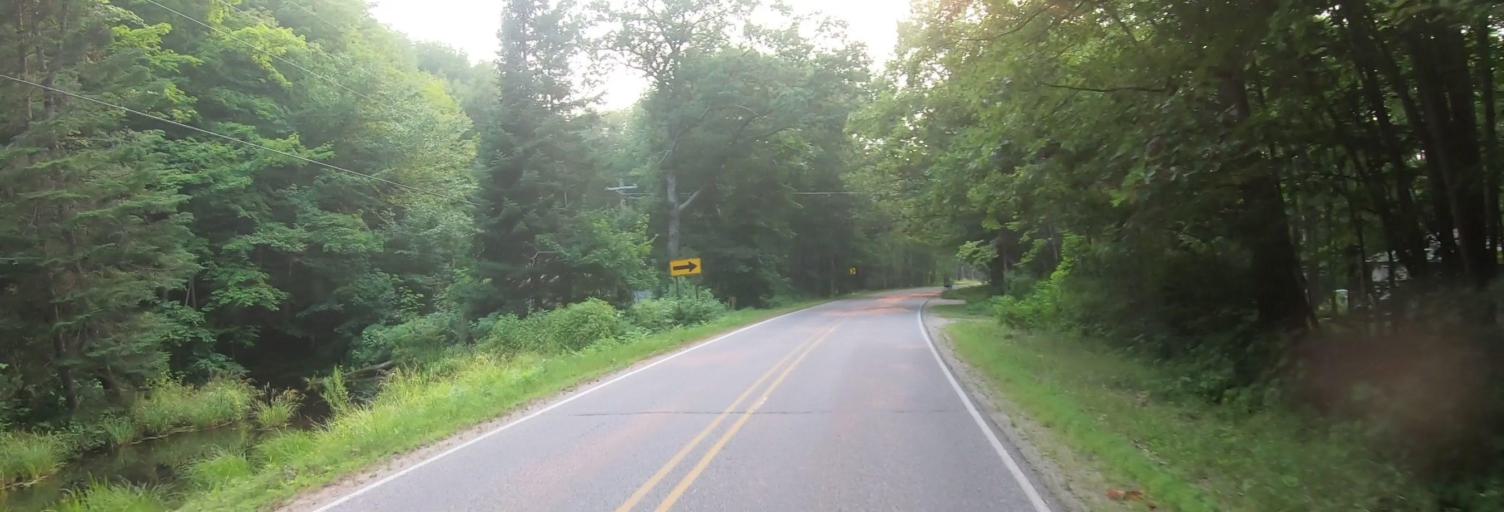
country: US
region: Michigan
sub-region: Chippewa County
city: Sault Ste. Marie
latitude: 46.4813
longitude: -84.6559
